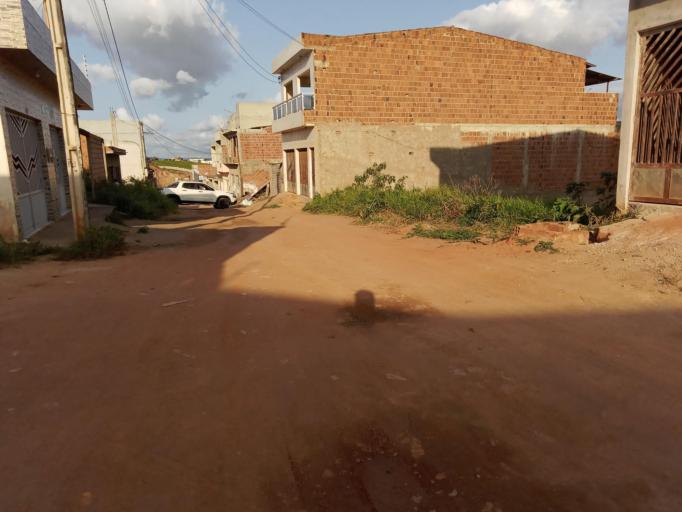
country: BR
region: Pernambuco
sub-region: Vitoria De Santo Antao
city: Vitoria de Santo Antao
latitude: -8.1253
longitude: -35.2798
